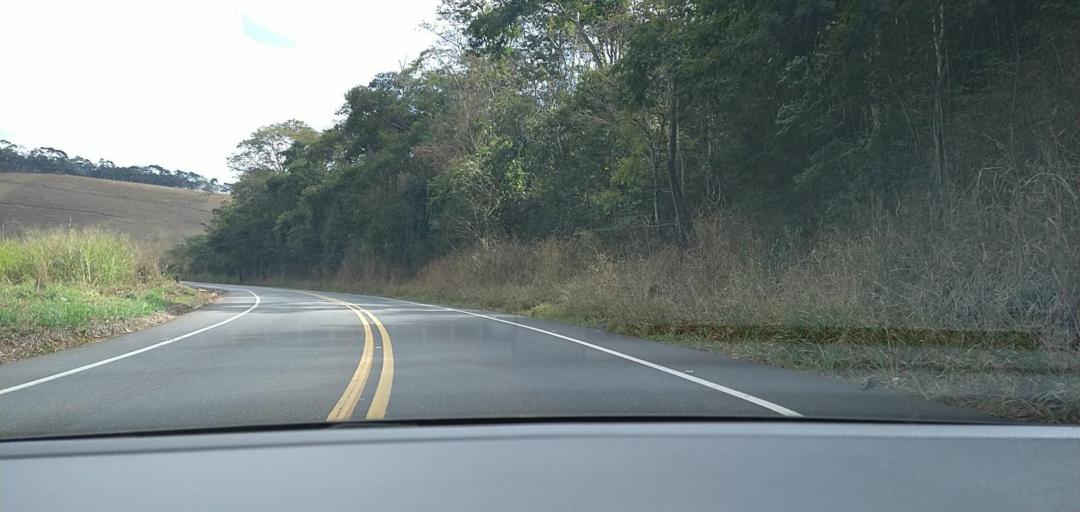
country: BR
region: Minas Gerais
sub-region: Ponte Nova
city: Ponte Nova
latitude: -20.4949
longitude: -42.8776
